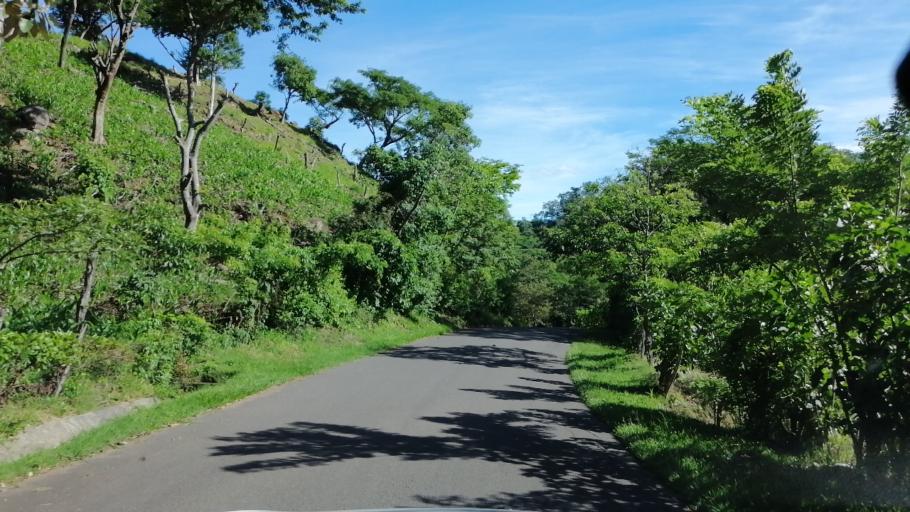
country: SV
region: Morazan
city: Corinto
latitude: 13.8003
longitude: -88.0032
